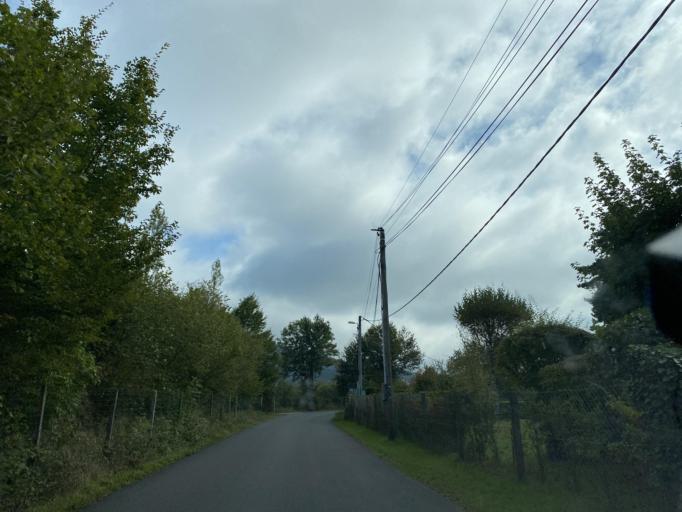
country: FR
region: Auvergne
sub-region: Departement du Puy-de-Dome
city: Peschadoires
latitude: 45.8362
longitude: 3.5340
